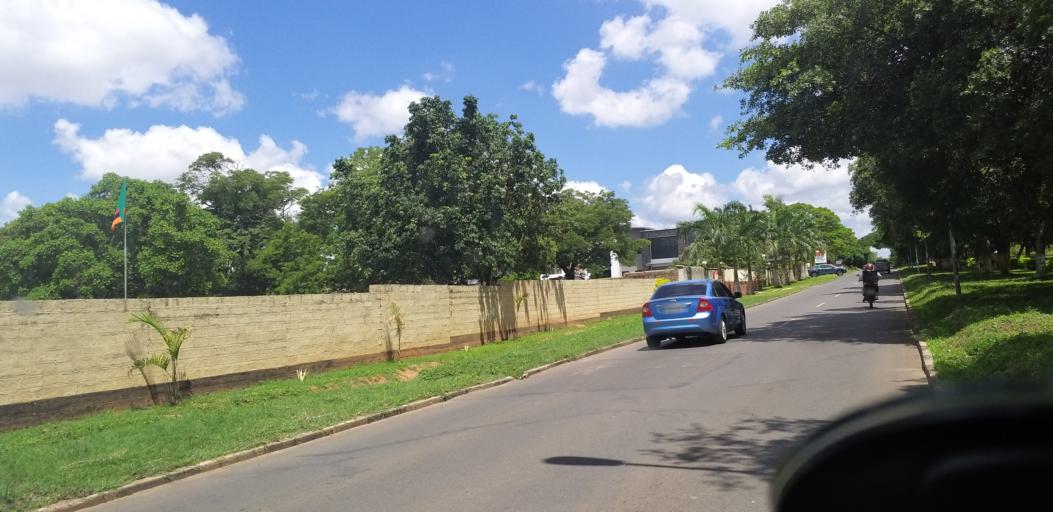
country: ZM
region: Lusaka
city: Lusaka
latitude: -15.4269
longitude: 28.3168
